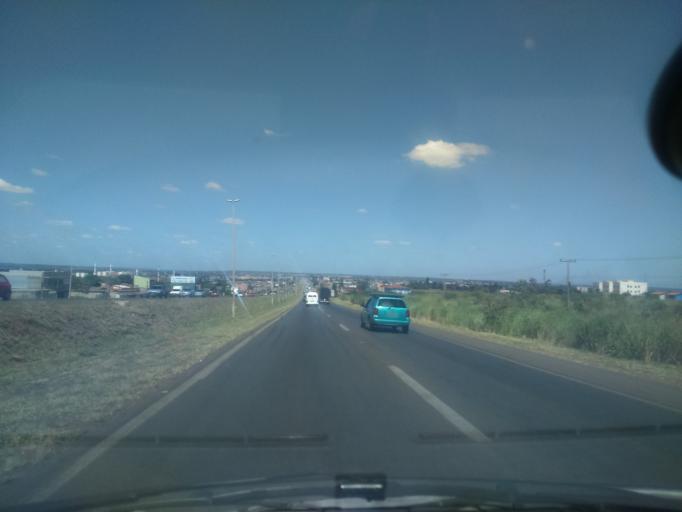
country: BR
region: Goias
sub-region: Luziania
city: Luziania
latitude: -16.1040
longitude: -47.9755
